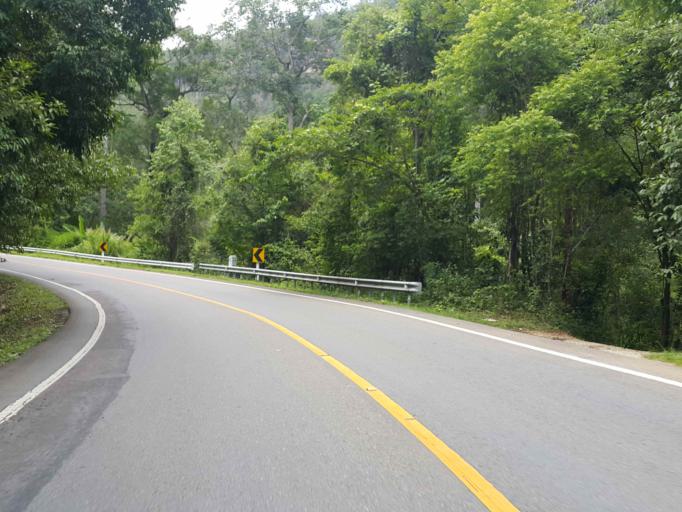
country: TH
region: Chiang Mai
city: Chom Thong
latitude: 18.5332
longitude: 98.6053
